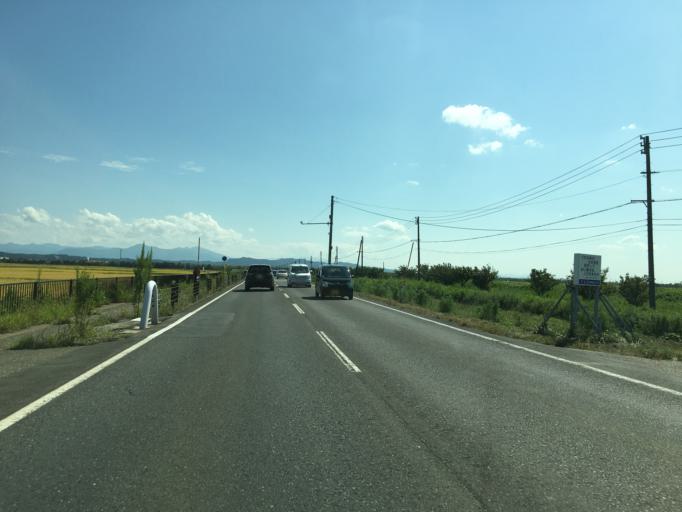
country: JP
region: Niigata
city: Niitsu-honcho
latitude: 37.8308
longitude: 139.0972
